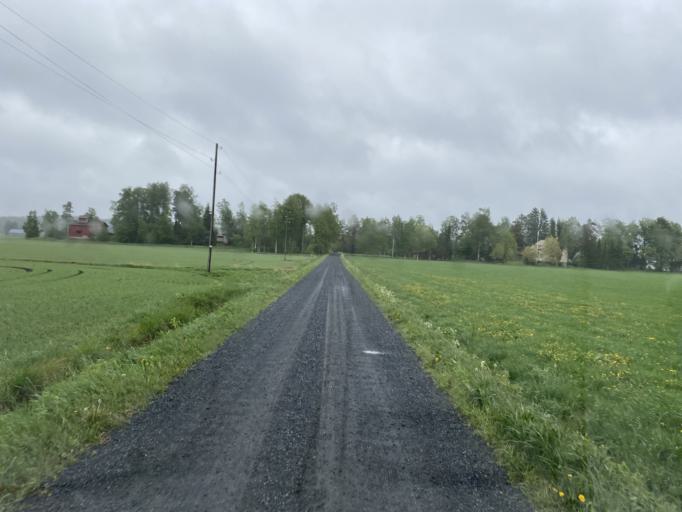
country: FI
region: Pirkanmaa
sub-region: Etelae-Pirkanmaa
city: Urjala
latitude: 60.9471
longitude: 23.5439
